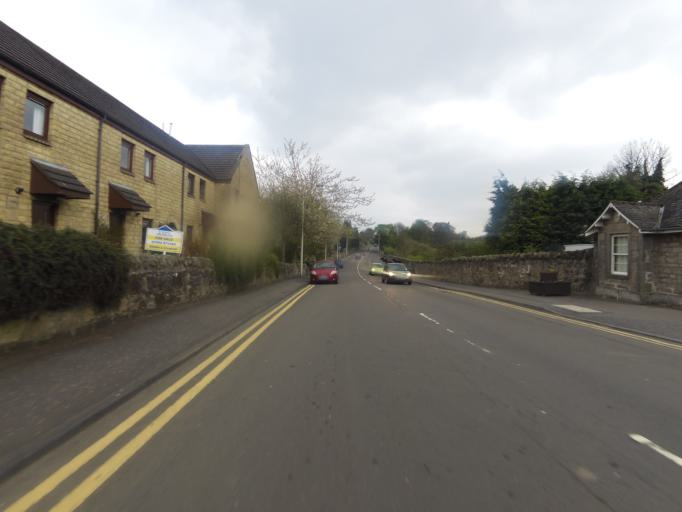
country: GB
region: Scotland
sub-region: Fife
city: Aberdour
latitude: 56.0560
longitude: -3.2982
